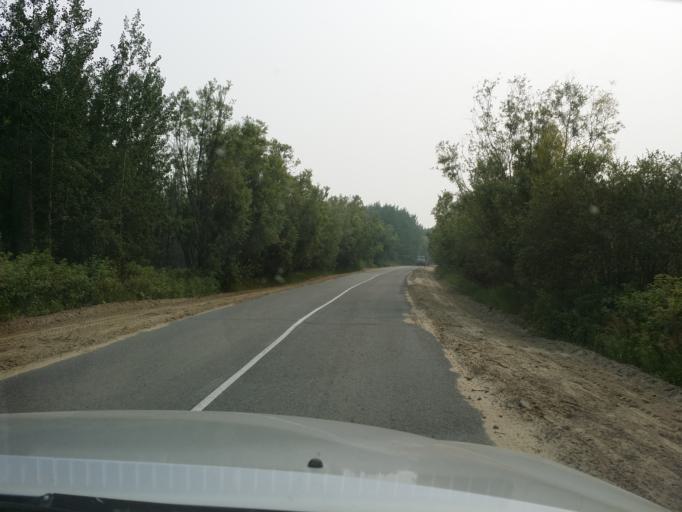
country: RU
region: Khanty-Mansiyskiy Avtonomnyy Okrug
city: Megion
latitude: 60.9824
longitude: 76.2974
